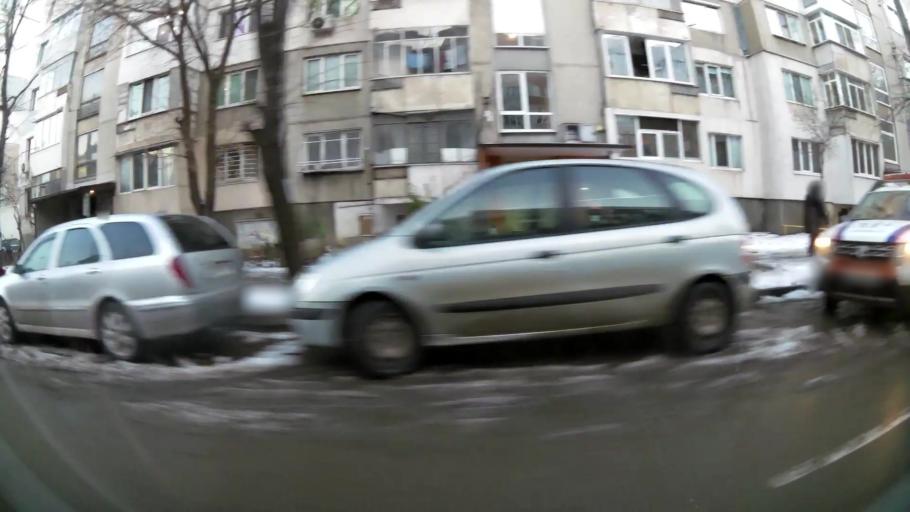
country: BG
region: Sofia-Capital
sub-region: Stolichna Obshtina
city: Sofia
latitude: 42.6883
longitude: 23.3712
